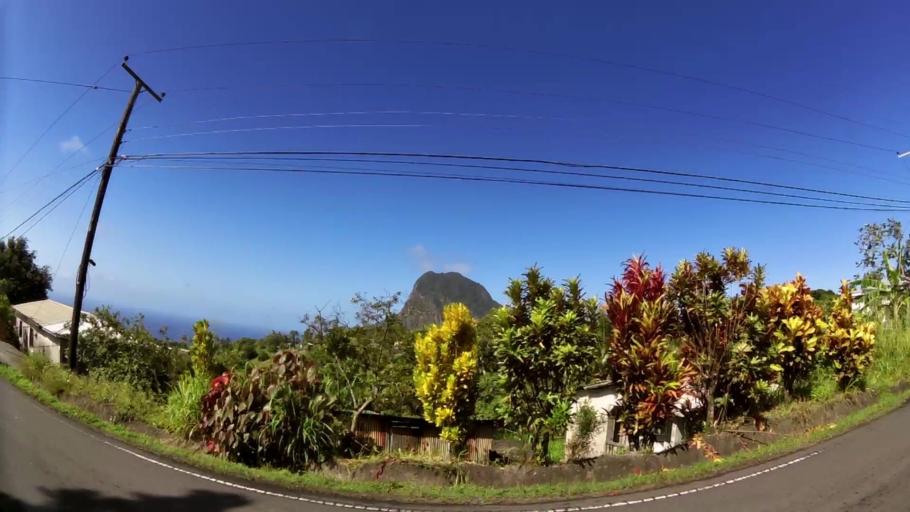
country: LC
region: Choiseul Quarter
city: Choiseul
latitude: 13.8089
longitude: -61.0396
